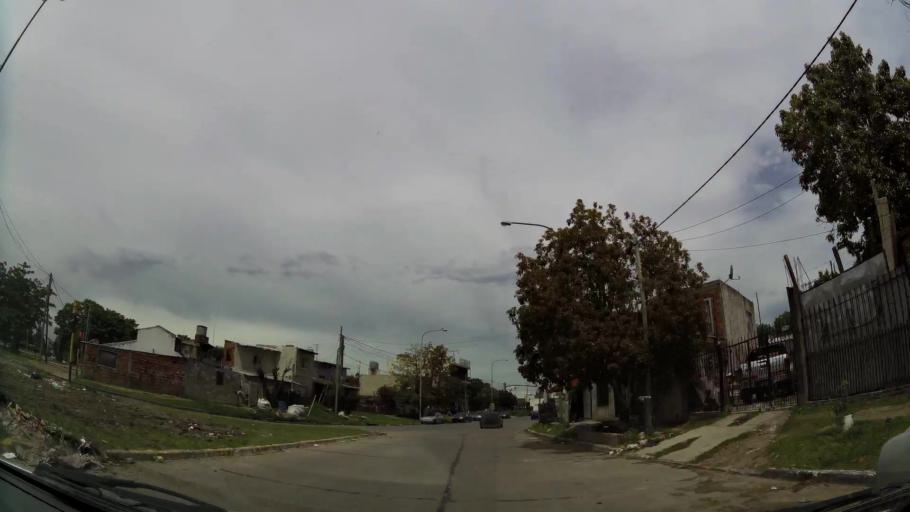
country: AR
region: Buenos Aires
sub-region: Partido de Quilmes
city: Quilmes
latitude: -34.7685
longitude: -58.2332
